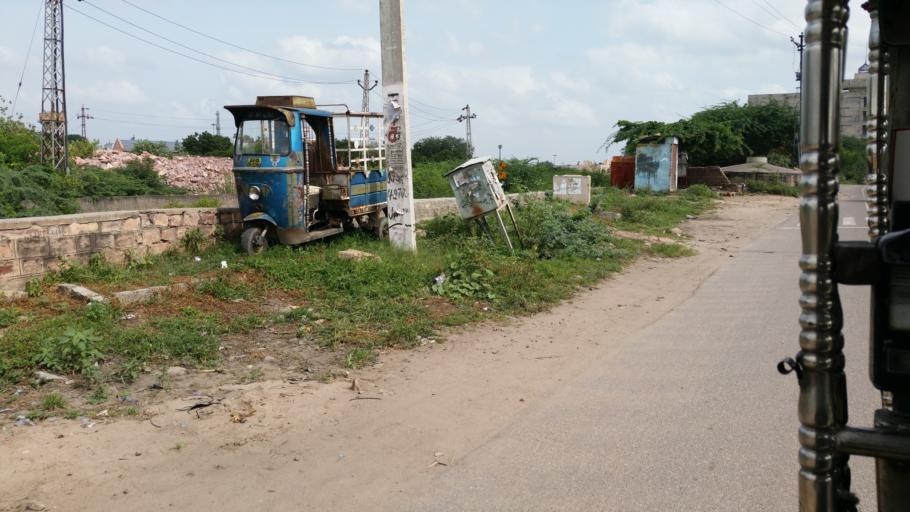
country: IN
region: Rajasthan
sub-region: Jodhpur
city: Jodhpur
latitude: 26.3238
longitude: 73.0446
